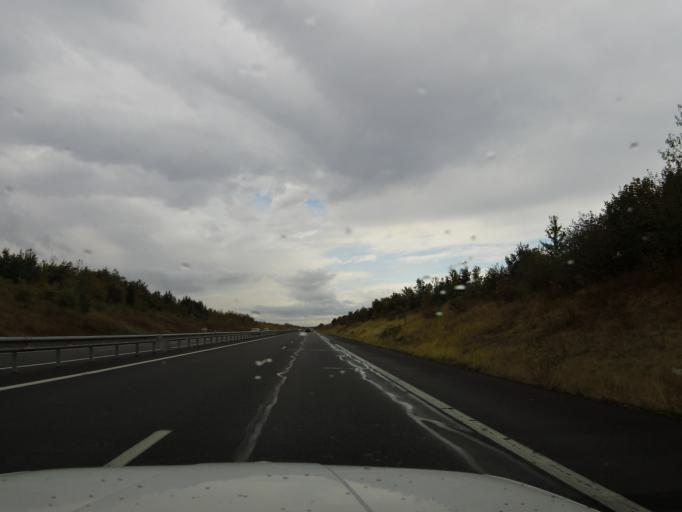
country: FR
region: Rhone-Alpes
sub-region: Departement de l'Isere
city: Janneyrias
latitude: 45.7417
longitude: 5.0956
